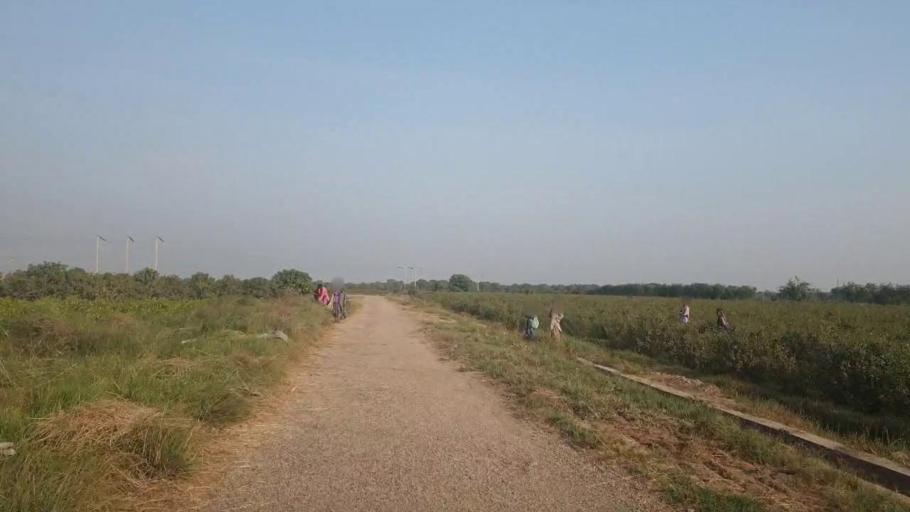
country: PK
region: Sindh
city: Tando Jam
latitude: 25.4224
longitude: 68.4725
